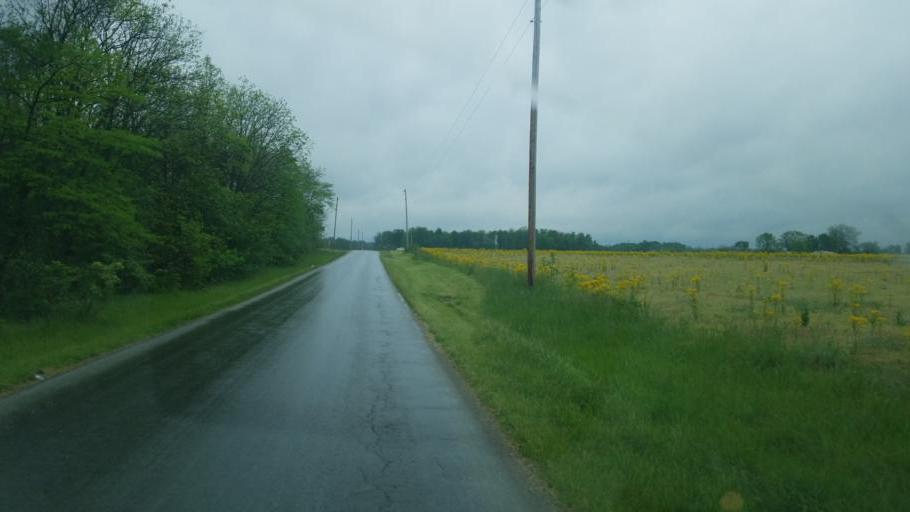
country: US
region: Ohio
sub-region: Highland County
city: Greenfield
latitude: 39.3233
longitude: -83.4236
